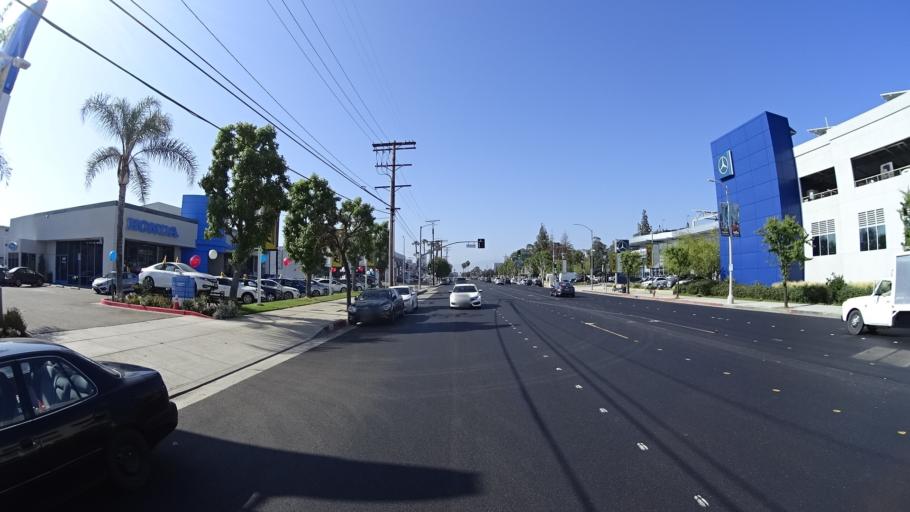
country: US
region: California
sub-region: Los Angeles County
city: Sherman Oaks
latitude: 34.1679
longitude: -118.4487
